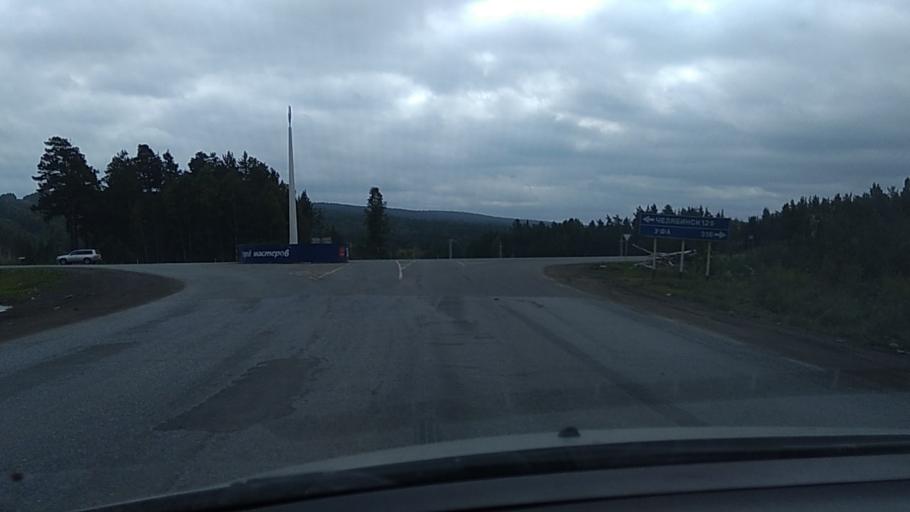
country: RU
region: Chelyabinsk
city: Zlatoust
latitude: 55.0566
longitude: 59.6968
